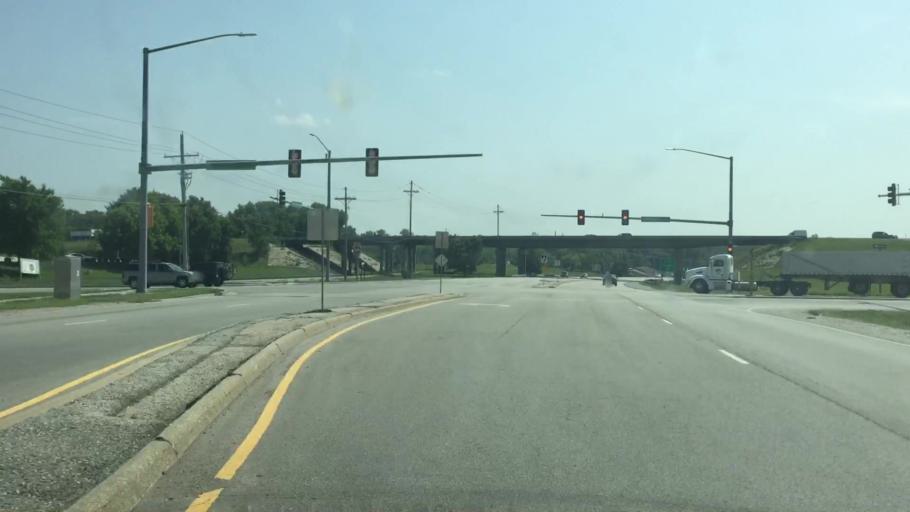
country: US
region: Kansas
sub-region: Johnson County
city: De Soto
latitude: 38.9629
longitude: -94.9831
